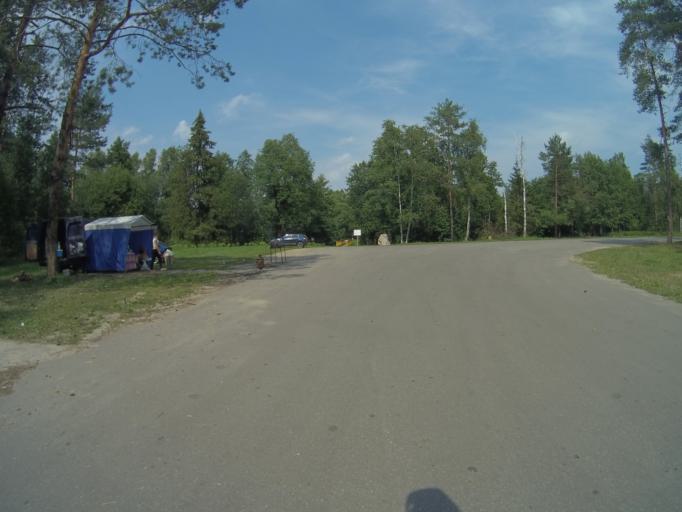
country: RU
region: Vladimir
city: Muromtsevo
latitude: 55.9582
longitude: 40.9589
